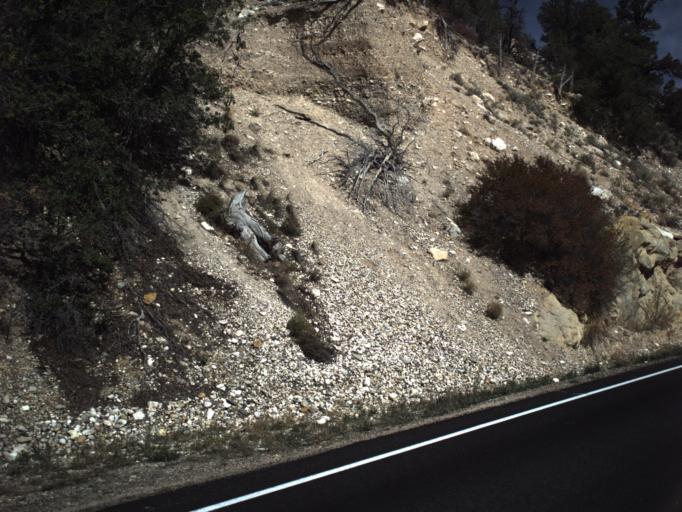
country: US
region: Utah
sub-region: Garfield County
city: Panguitch
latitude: 37.7165
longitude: -111.7841
